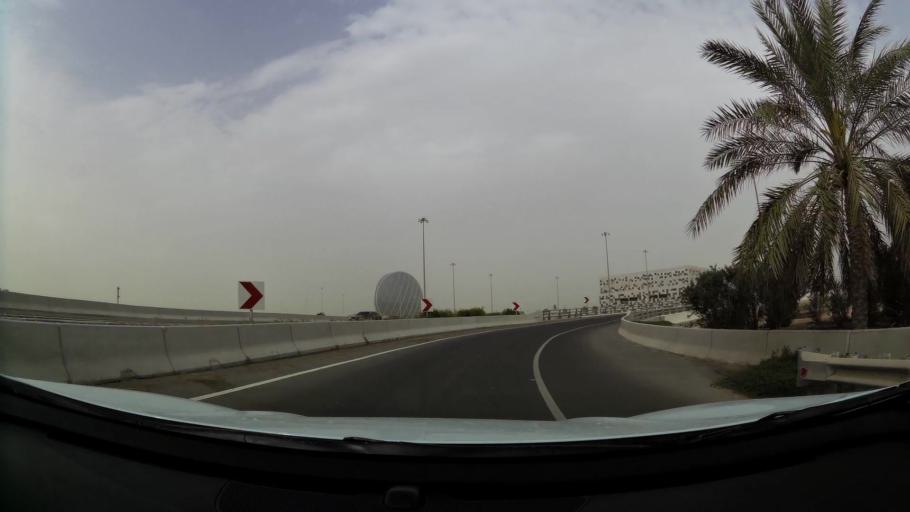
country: AE
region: Abu Dhabi
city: Abu Dhabi
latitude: 24.4391
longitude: 54.5848
